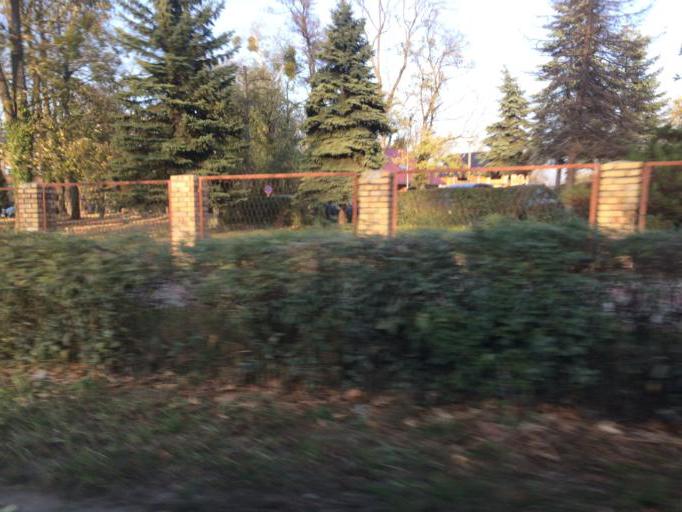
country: PL
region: Opole Voivodeship
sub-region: Powiat strzelecki
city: Strzelce Opolskie
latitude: 50.5135
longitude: 18.2916
